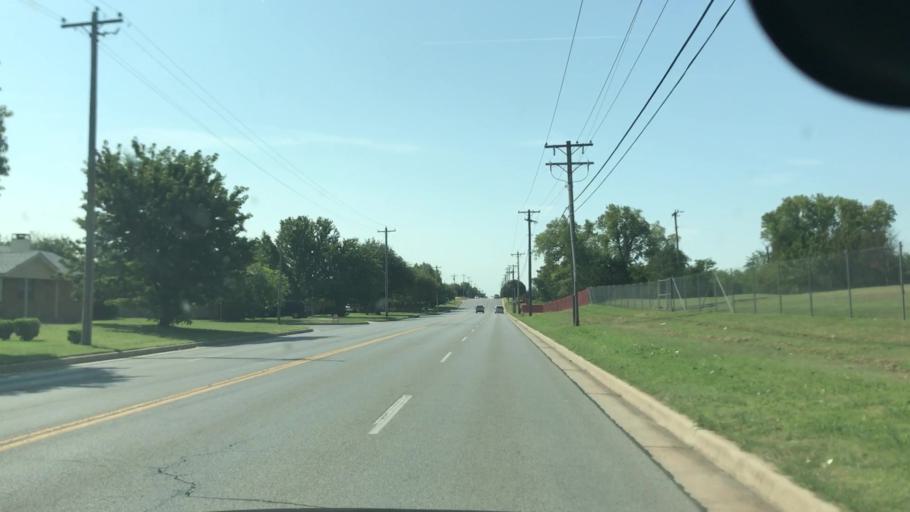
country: US
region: Oklahoma
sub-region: Cleveland County
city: Moore
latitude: 35.3587
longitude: -97.5122
